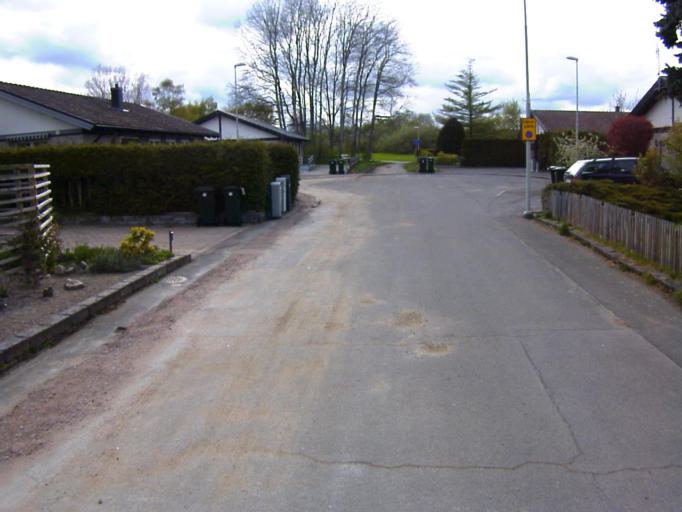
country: SE
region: Skane
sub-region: Kristianstads Kommun
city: Kristianstad
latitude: 56.0489
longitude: 14.1883
